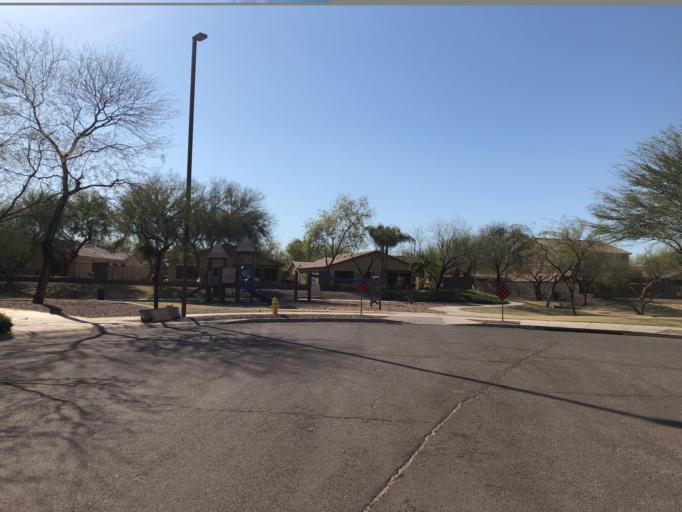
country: US
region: Arizona
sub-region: Maricopa County
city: Queen Creek
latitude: 33.2713
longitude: -111.7005
